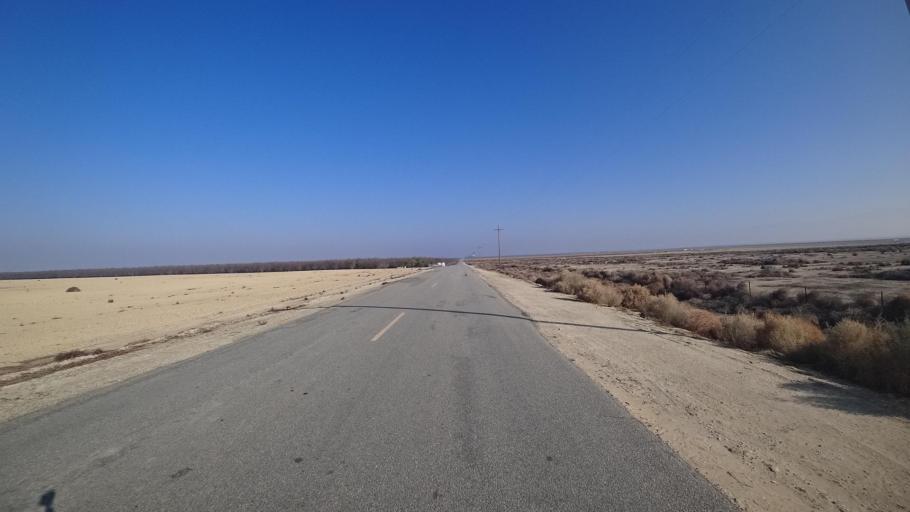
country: US
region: California
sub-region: Kern County
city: Maricopa
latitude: 35.1012
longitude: -119.3619
